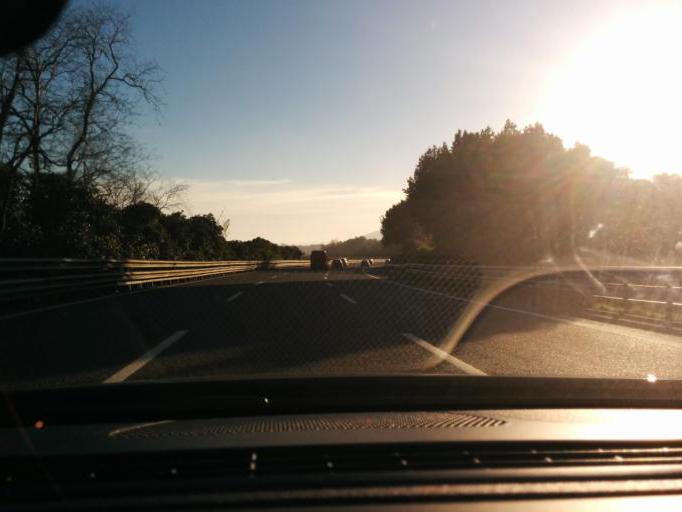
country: IT
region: Liguria
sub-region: Provincia di Genova
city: Arenzano
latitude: 44.4124
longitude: 8.6978
